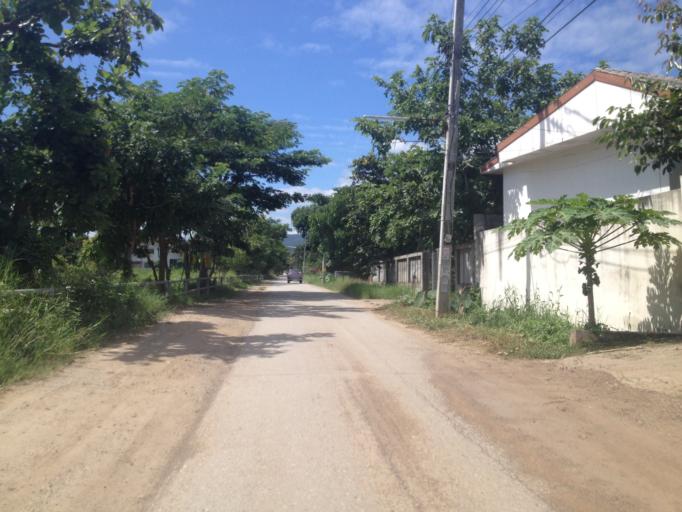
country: TH
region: Chiang Mai
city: Chiang Mai
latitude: 18.7608
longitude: 98.9537
